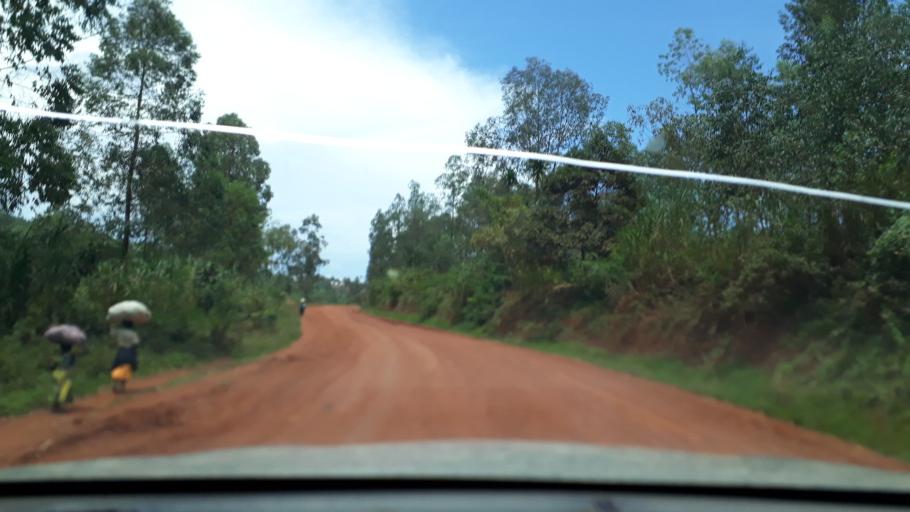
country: CD
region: Eastern Province
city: Bunia
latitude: 1.7230
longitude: 30.2968
